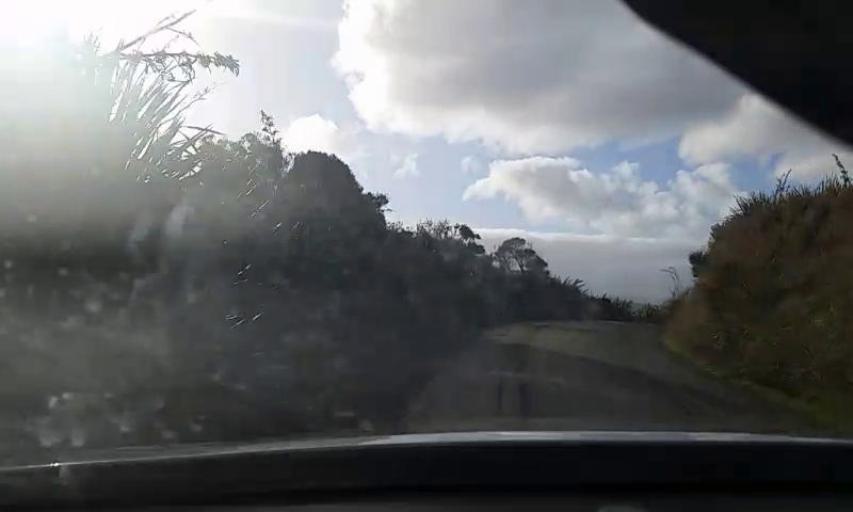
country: NZ
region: Otago
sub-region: Clutha District
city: Papatowai
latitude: -46.6510
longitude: 169.0984
